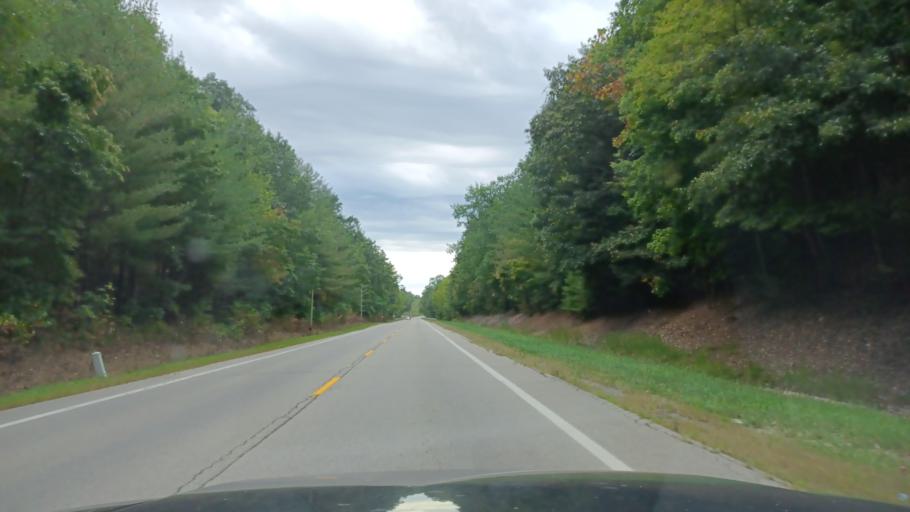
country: US
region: Ohio
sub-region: Vinton County
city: McArthur
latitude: 39.2368
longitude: -82.4108
